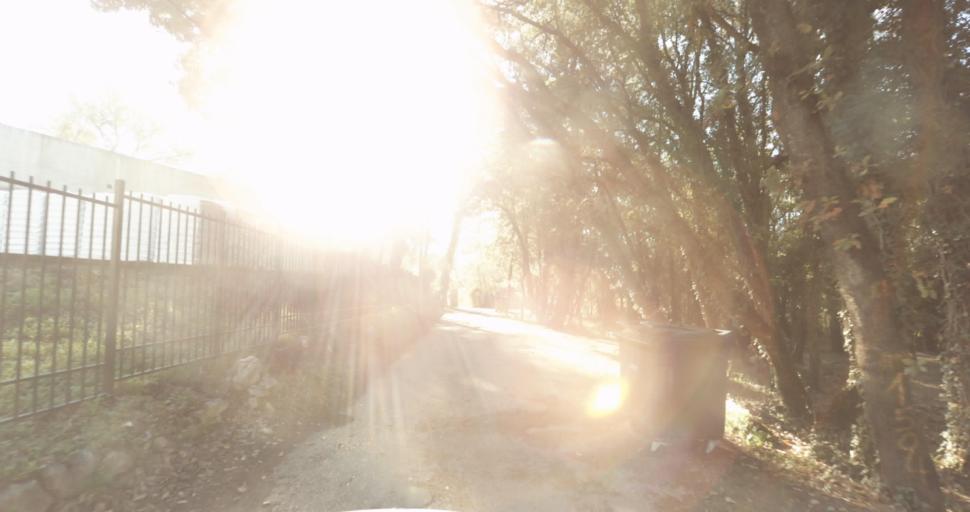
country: FR
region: Provence-Alpes-Cote d'Azur
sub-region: Departement des Alpes-Maritimes
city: Vence
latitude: 43.7135
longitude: 7.0859
